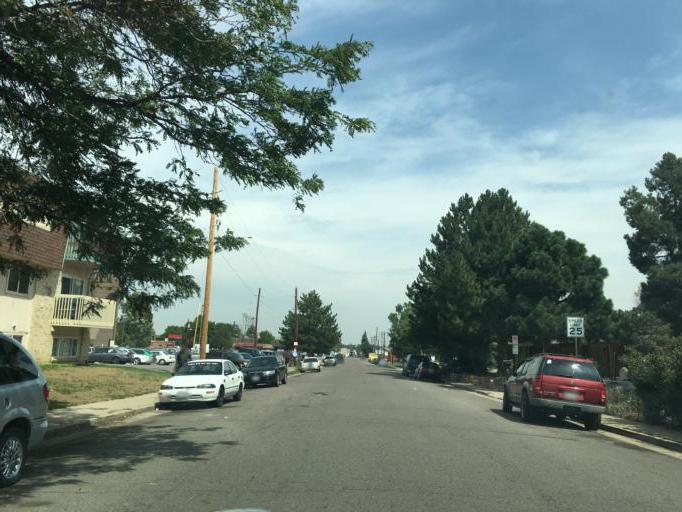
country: US
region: Colorado
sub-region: Adams County
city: Aurora
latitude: 39.7376
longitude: -104.8078
